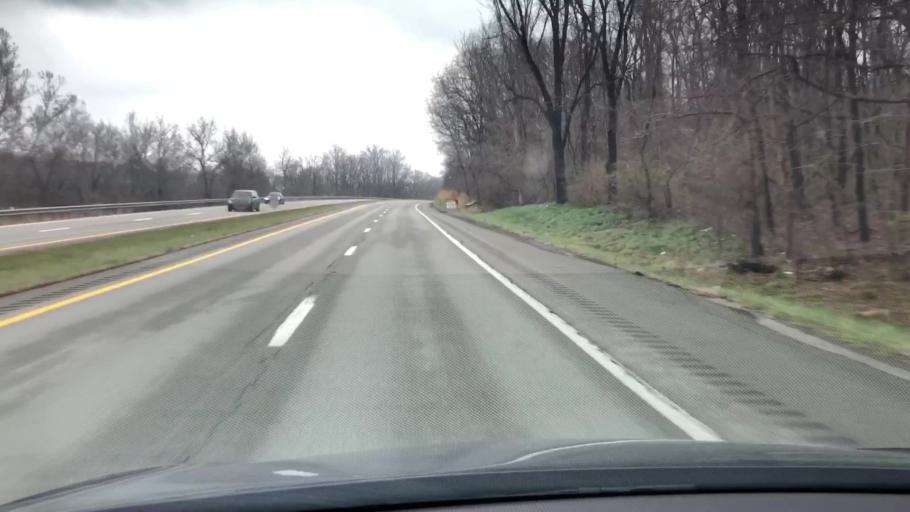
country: US
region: Pennsylvania
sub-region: Westmoreland County
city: Scottdale
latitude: 40.0777
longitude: -79.5625
